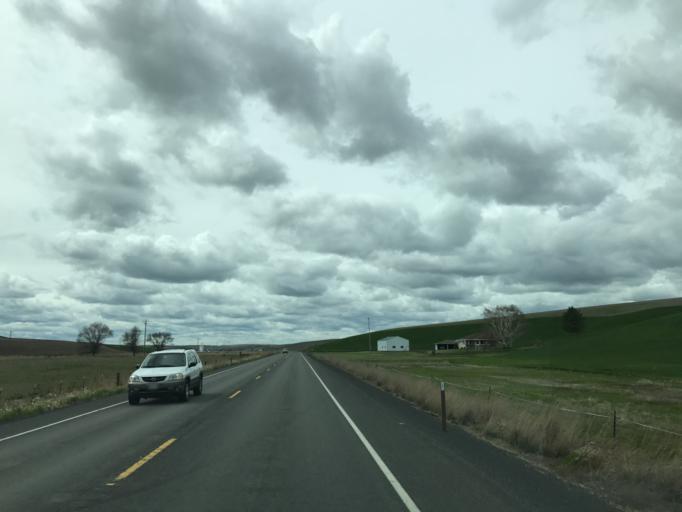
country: US
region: Washington
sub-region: Whitman County
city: Colfax
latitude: 46.8136
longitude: -117.5997
